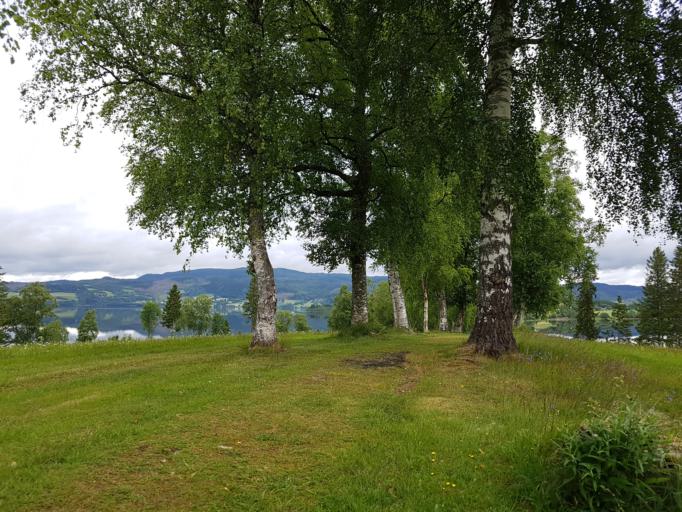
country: NO
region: Sor-Trondelag
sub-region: Selbu
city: Mebonden
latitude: 63.2337
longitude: 11.0291
